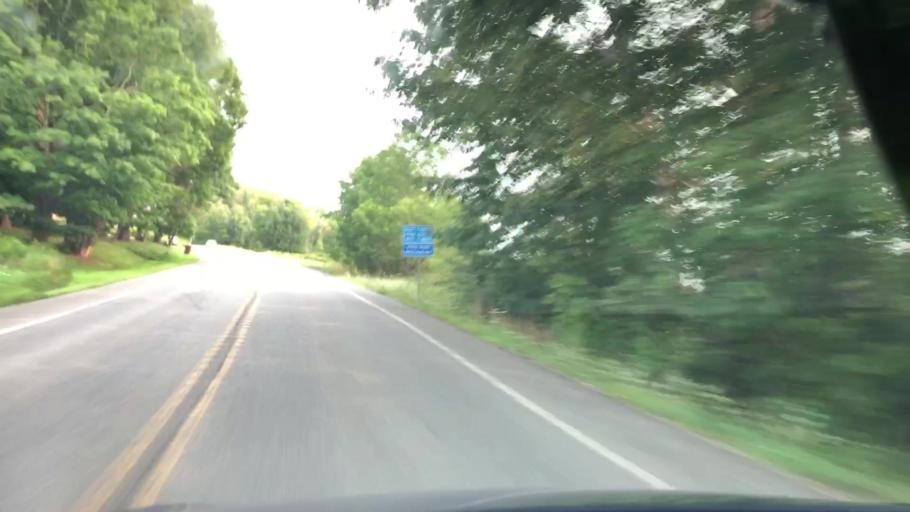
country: US
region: Pennsylvania
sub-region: Erie County
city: Union City
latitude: 41.8327
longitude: -79.8174
